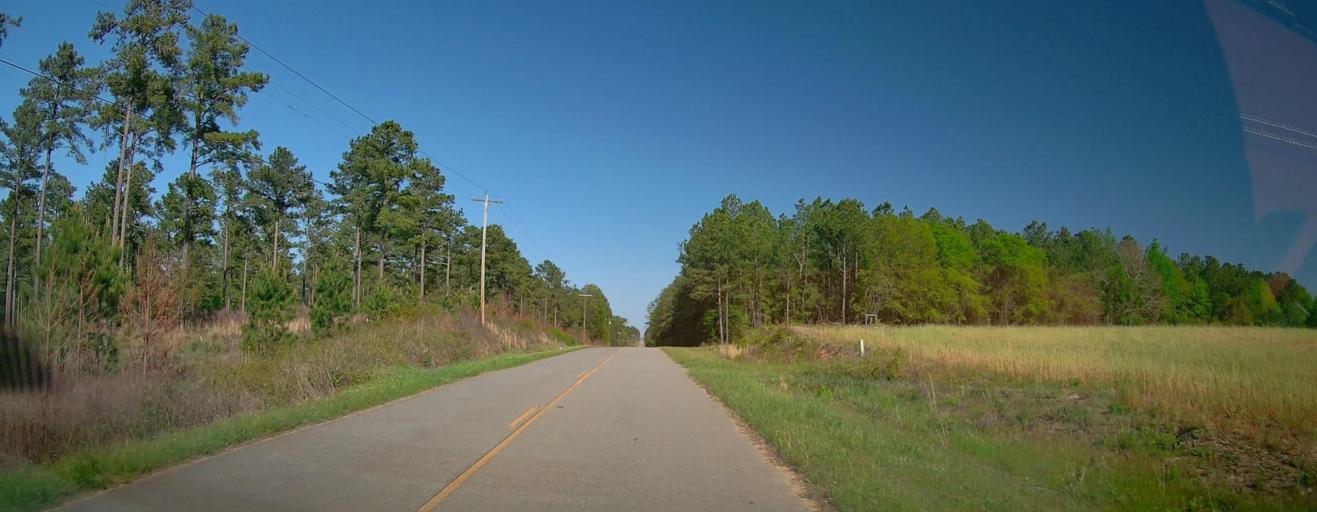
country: US
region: Georgia
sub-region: Pulaski County
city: Hawkinsville
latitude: 32.2405
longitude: -83.5431
